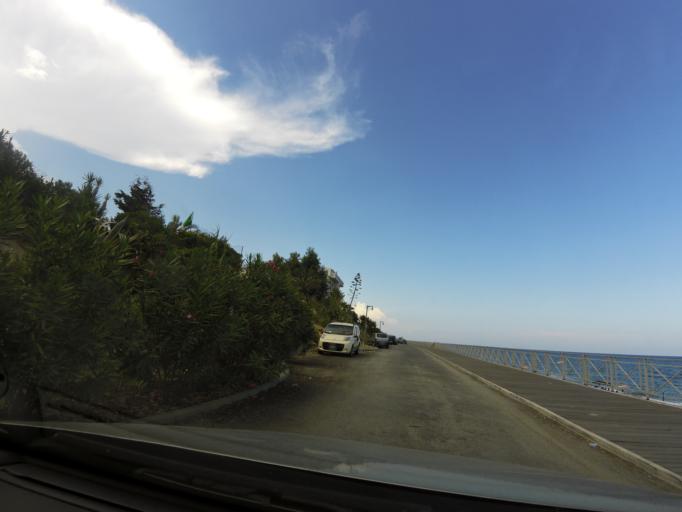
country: IT
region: Calabria
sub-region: Provincia di Reggio Calabria
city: Monasterace Marina
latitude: 38.4415
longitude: 16.5777
